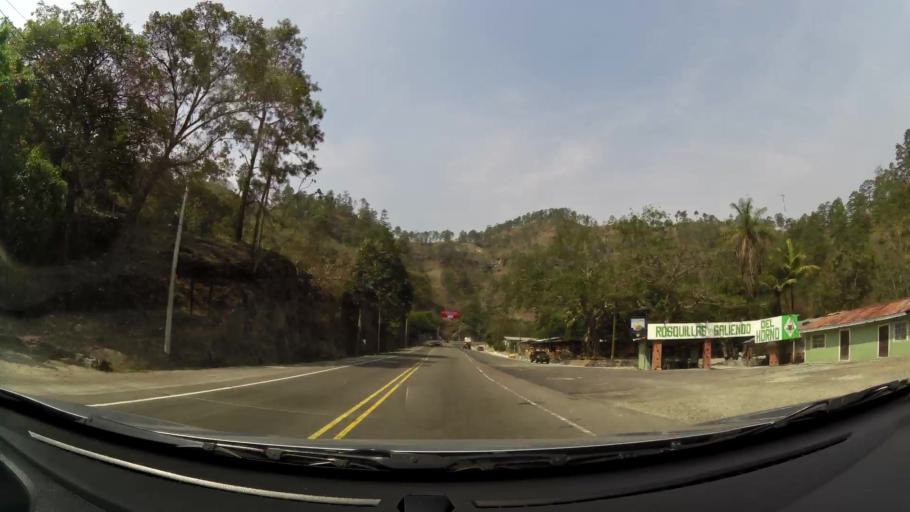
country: HN
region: Comayagua
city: Potrerillos
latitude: 14.5323
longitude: -87.8037
